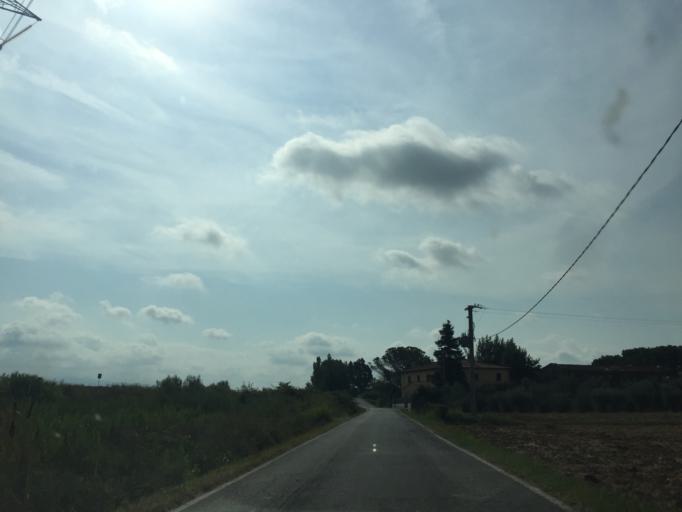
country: IT
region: Tuscany
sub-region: Provincia di Pistoia
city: Cintolese
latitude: 43.8485
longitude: 10.8095
